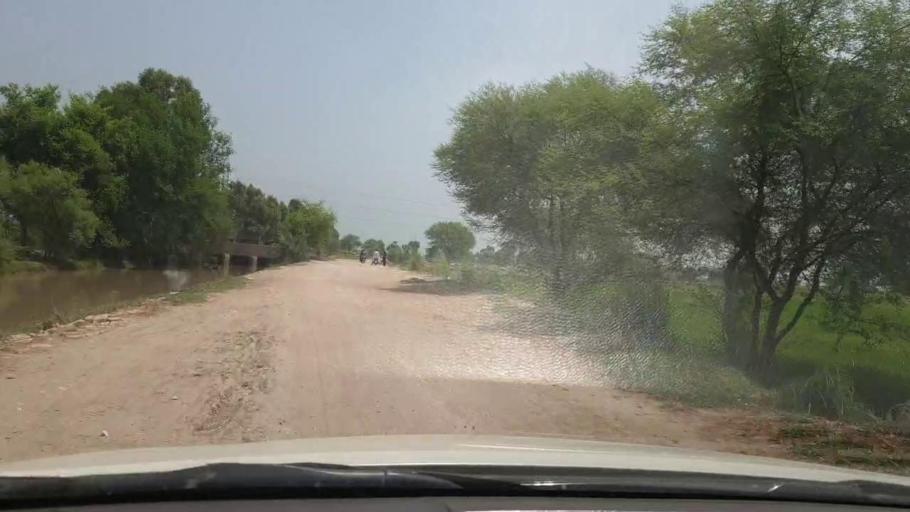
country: PK
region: Sindh
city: Shikarpur
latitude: 28.0525
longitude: 68.6067
